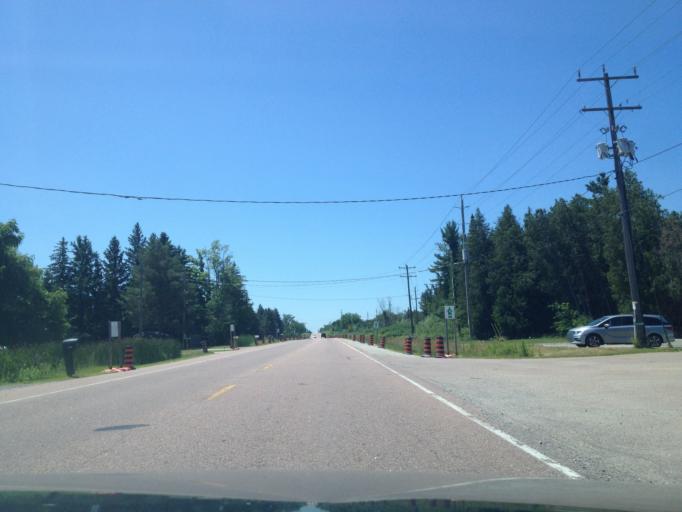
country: CA
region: Ontario
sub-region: Halton
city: Milton
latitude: 43.6697
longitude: -79.9924
